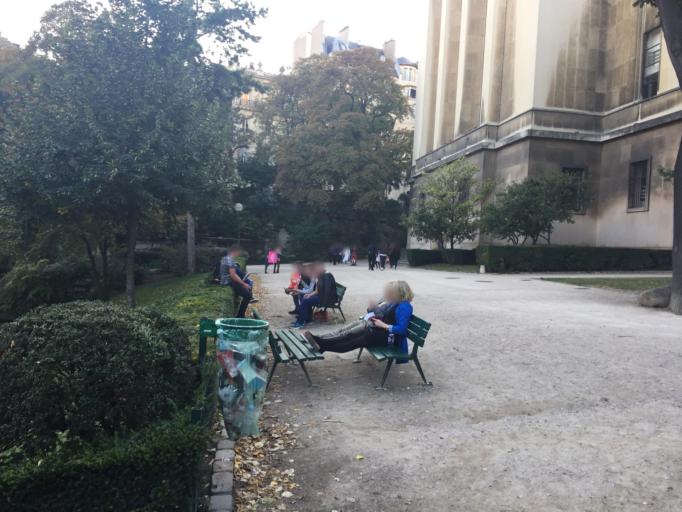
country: FR
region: Ile-de-France
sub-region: Departement des Hauts-de-Seine
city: Neuilly-sur-Seine
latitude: 48.8606
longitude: 2.2878
